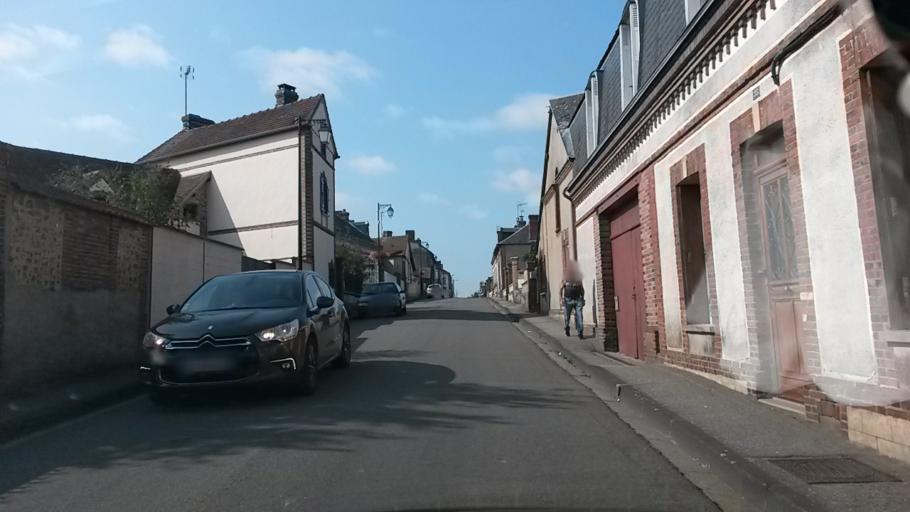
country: FR
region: Haute-Normandie
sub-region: Departement de l'Eure
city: Damville
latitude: 48.8690
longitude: 1.0733
